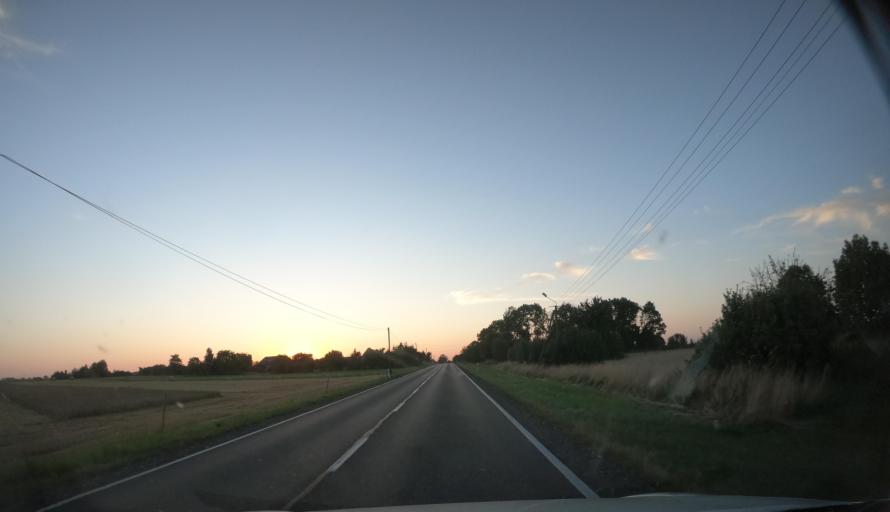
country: PL
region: Kujawsko-Pomorskie
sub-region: Powiat bydgoski
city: Koronowo
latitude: 53.3311
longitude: 17.8940
